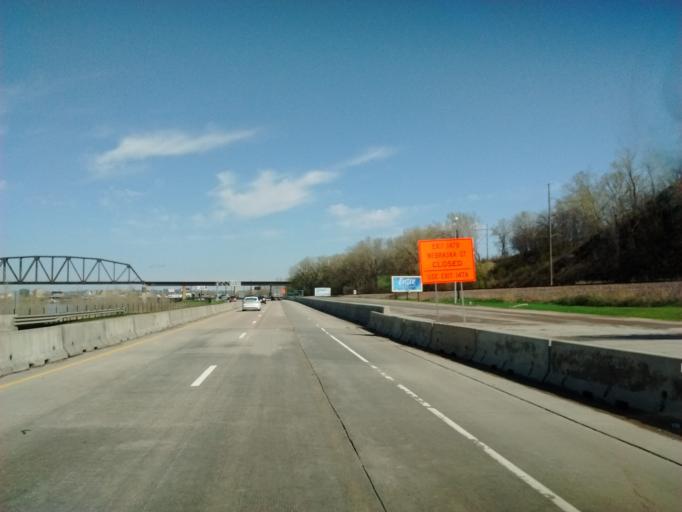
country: US
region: Nebraska
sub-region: Dakota County
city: South Sioux City
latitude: 42.4709
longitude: -96.3819
